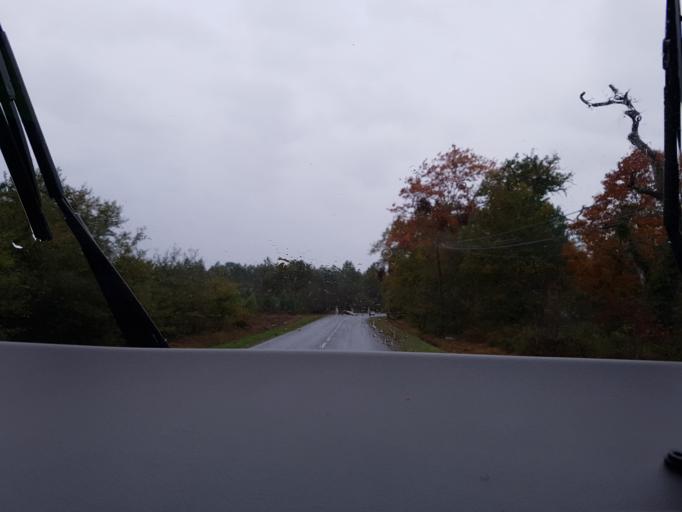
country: FR
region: Aquitaine
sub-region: Departement de la Gironde
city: Saint-Symphorien
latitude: 44.3324
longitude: -0.5925
